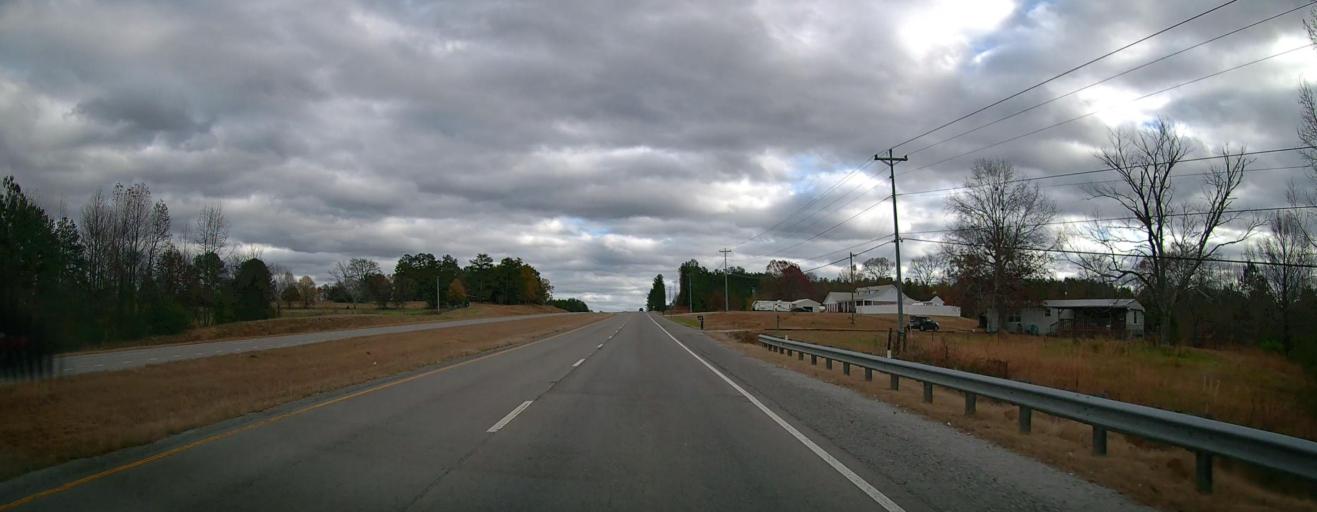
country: US
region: Alabama
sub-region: Lawrence County
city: Town Creek
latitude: 34.5811
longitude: -87.4112
